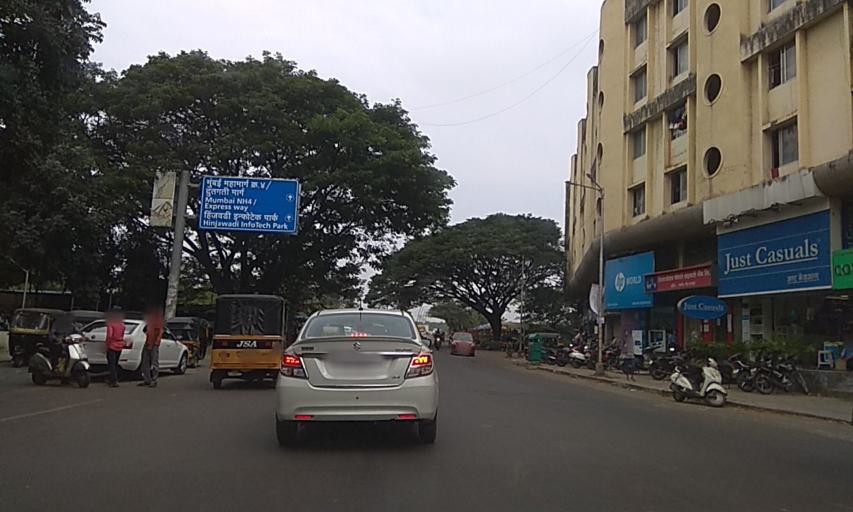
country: IN
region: Maharashtra
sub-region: Pune Division
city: Khadki
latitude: 18.5665
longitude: 73.8075
